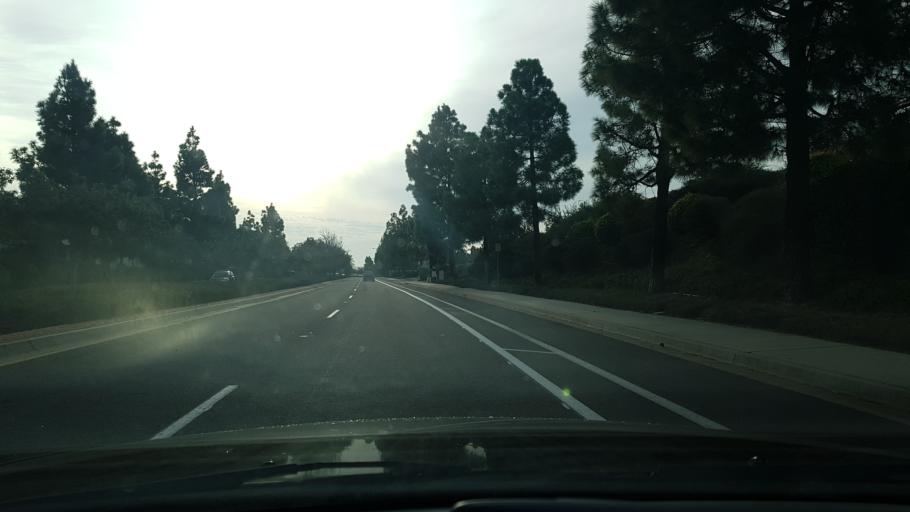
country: US
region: California
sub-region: San Diego County
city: Fairbanks Ranch
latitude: 32.9169
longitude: -117.1892
